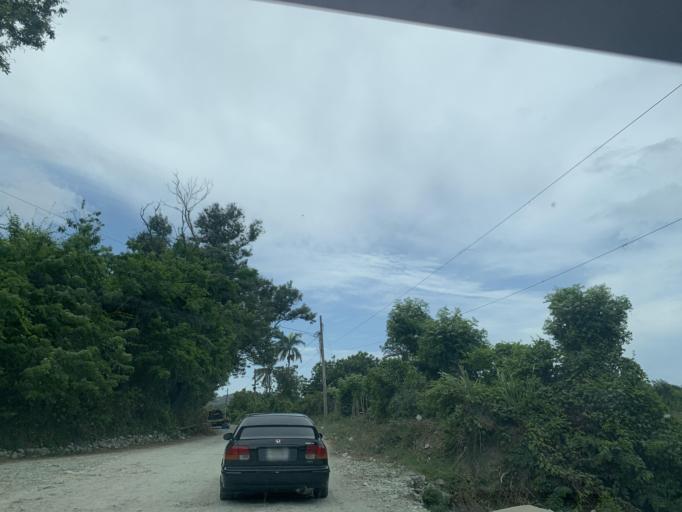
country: DO
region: Puerto Plata
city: Imbert
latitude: 19.8198
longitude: -70.7801
